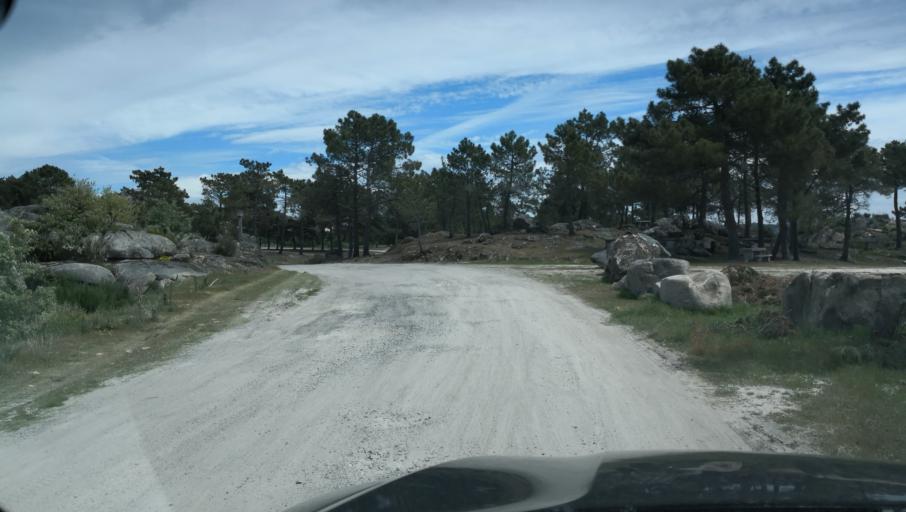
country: PT
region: Vila Real
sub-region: Vila Real
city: Vila Real
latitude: 41.3765
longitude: -7.6824
